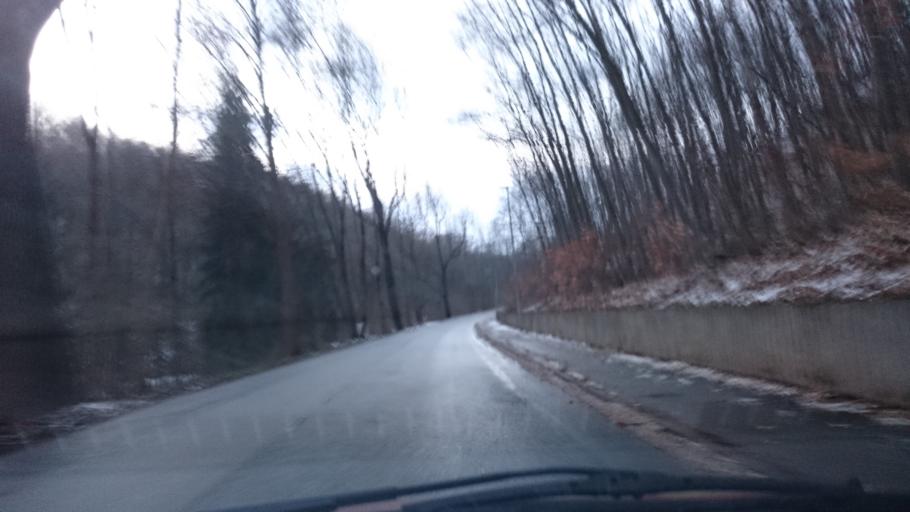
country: DE
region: Saxony
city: Wilkau-Hasslau
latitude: 50.7037
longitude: 12.5183
